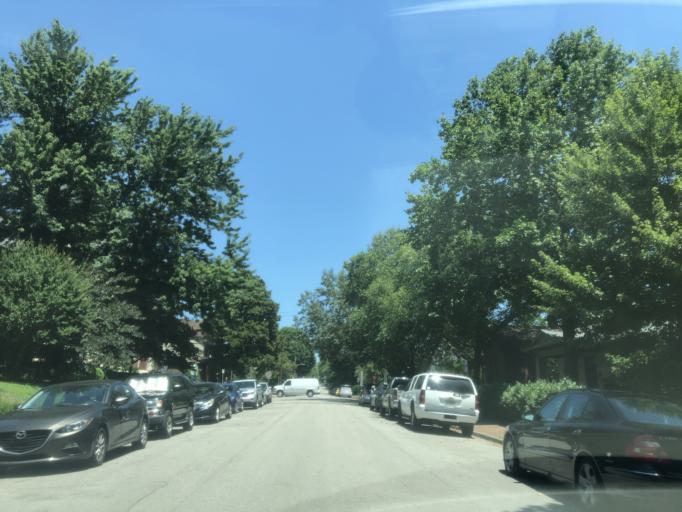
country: US
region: Tennessee
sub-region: Davidson County
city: Nashville
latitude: 36.1735
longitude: -86.7569
